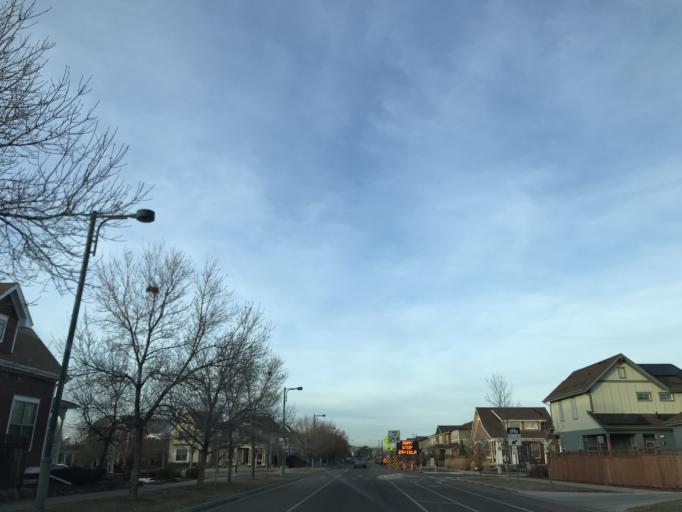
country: US
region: Colorado
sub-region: Adams County
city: Aurora
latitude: 39.7559
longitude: -104.8646
